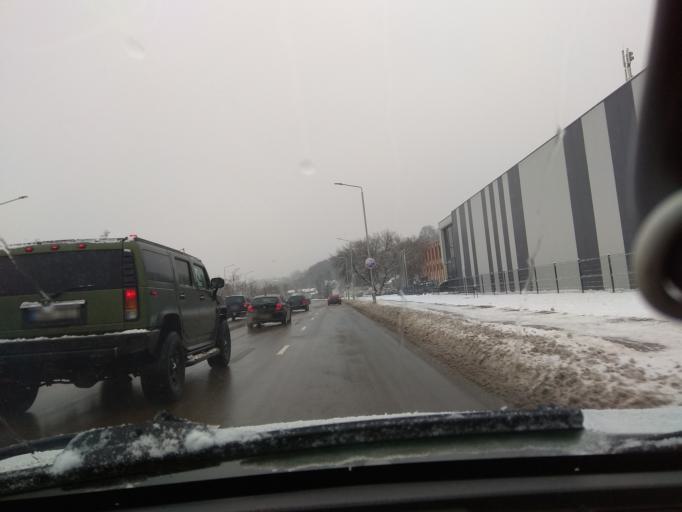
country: LT
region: Kauno apskritis
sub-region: Kaunas
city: Kaunas
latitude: 54.9073
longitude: 23.9033
